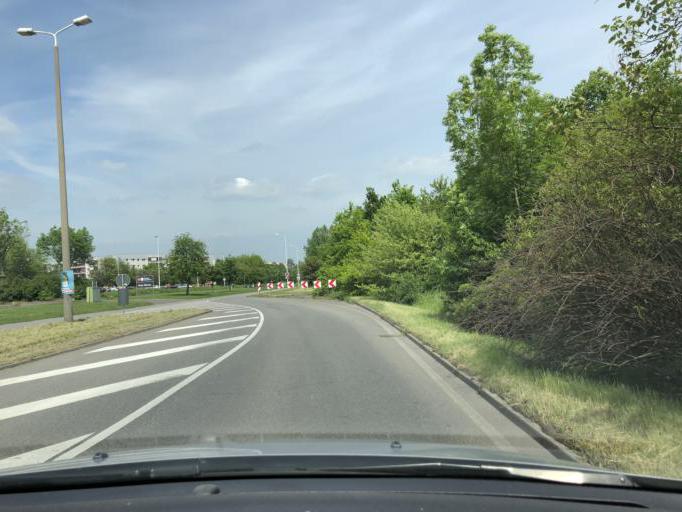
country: DE
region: Thuringia
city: Altenburg
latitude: 50.9967
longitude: 12.4254
